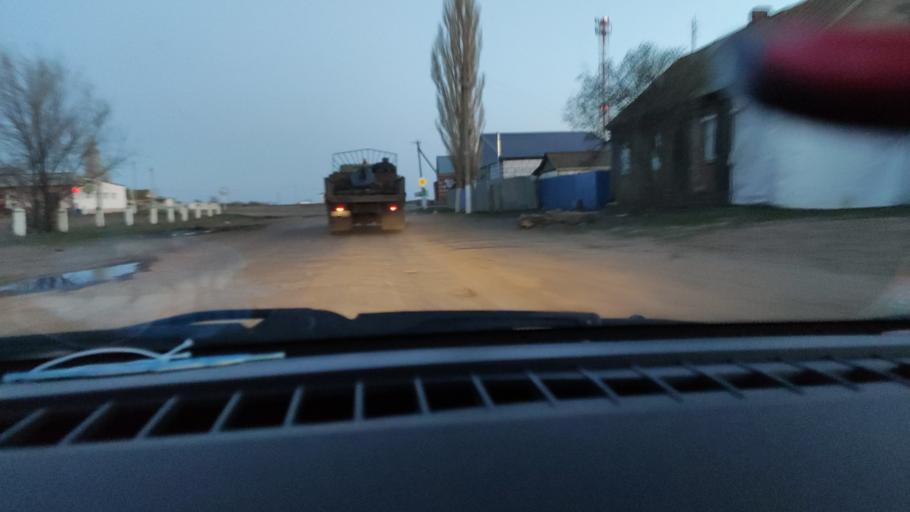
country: RU
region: Saratov
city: Rovnoye
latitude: 51.0216
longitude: 46.0930
